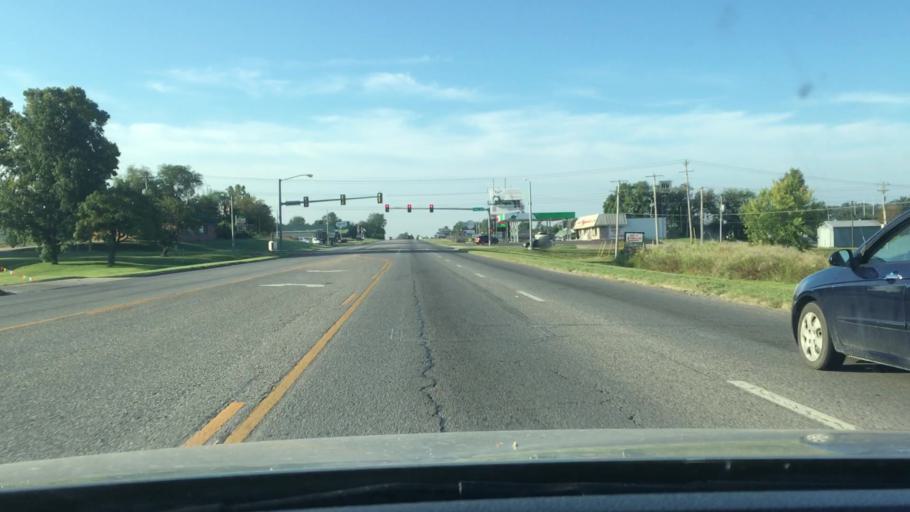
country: US
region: Oklahoma
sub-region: Cherokee County
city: Park Hill
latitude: 35.8720
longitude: -94.9763
